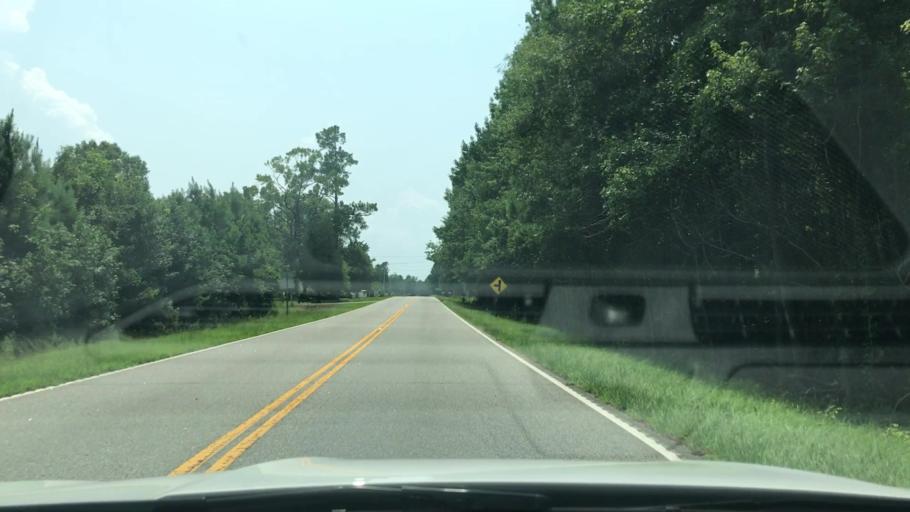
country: US
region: South Carolina
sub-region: Georgetown County
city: Georgetown
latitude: 33.5314
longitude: -79.2374
